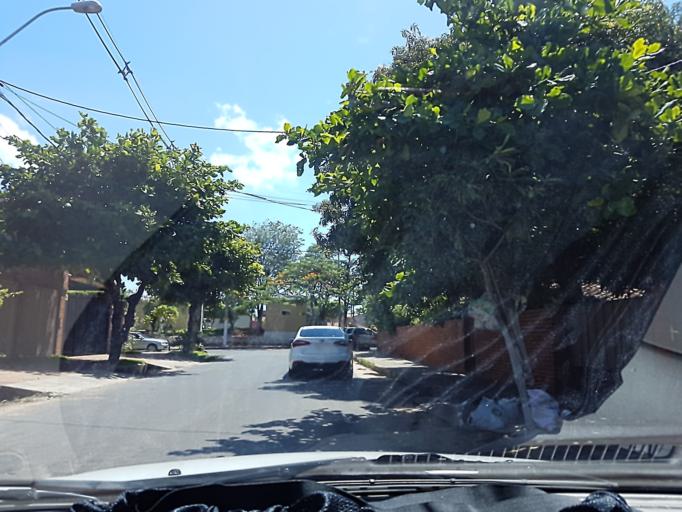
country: PY
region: Asuncion
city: Asuncion
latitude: -25.2720
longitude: -57.5755
